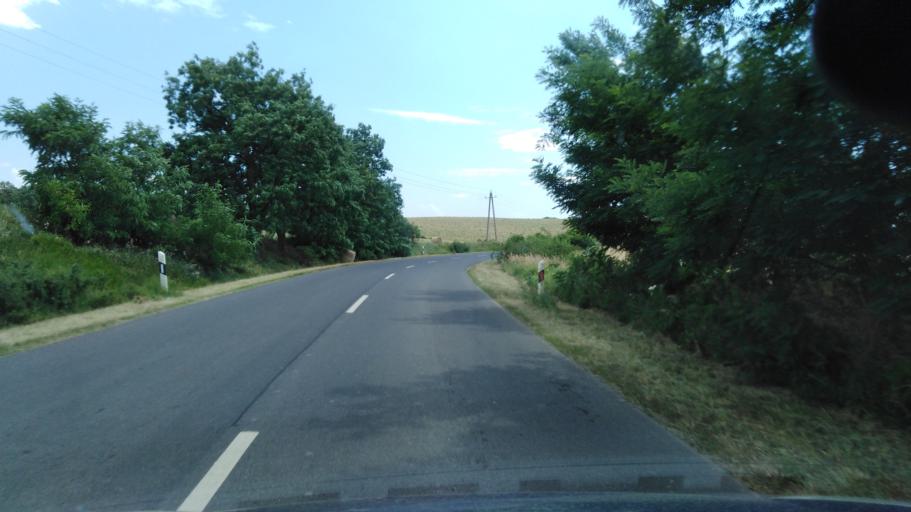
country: HU
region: Nograd
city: Szecseny
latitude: 48.1666
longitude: 19.5365
